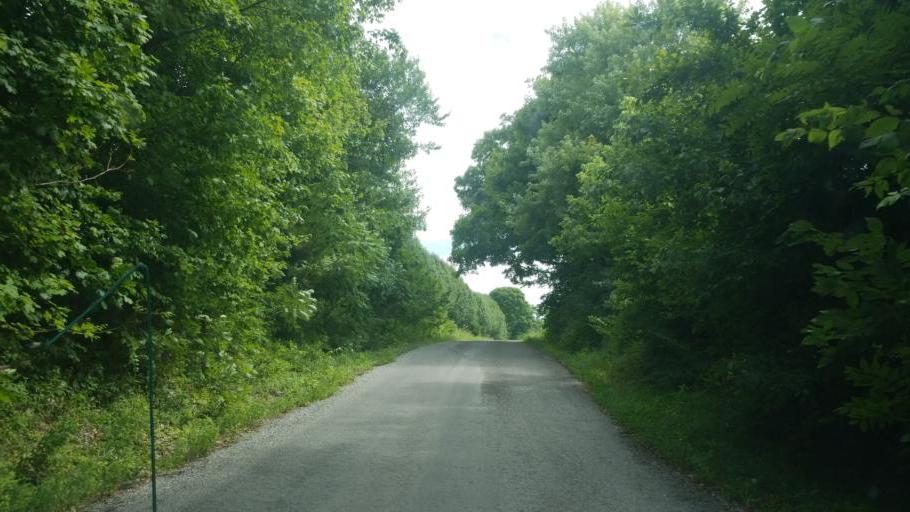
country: US
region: Illinois
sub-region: Union County
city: Cobden
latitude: 37.6178
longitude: -89.3711
